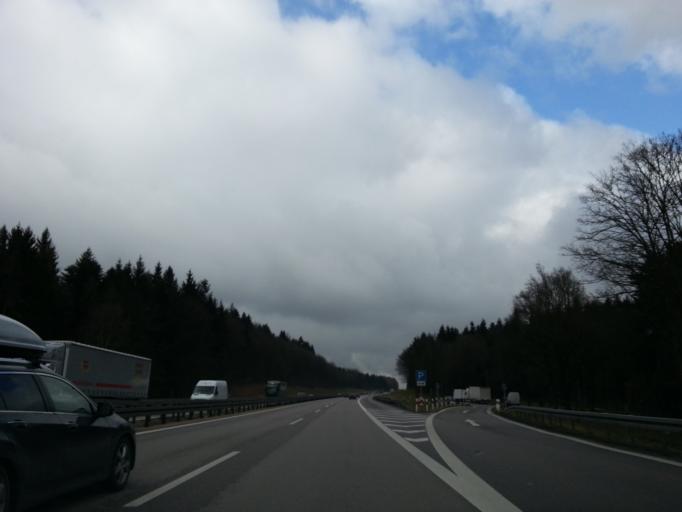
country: DE
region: Bavaria
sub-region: Upper Palatinate
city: Brunn
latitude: 49.1159
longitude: 11.8731
